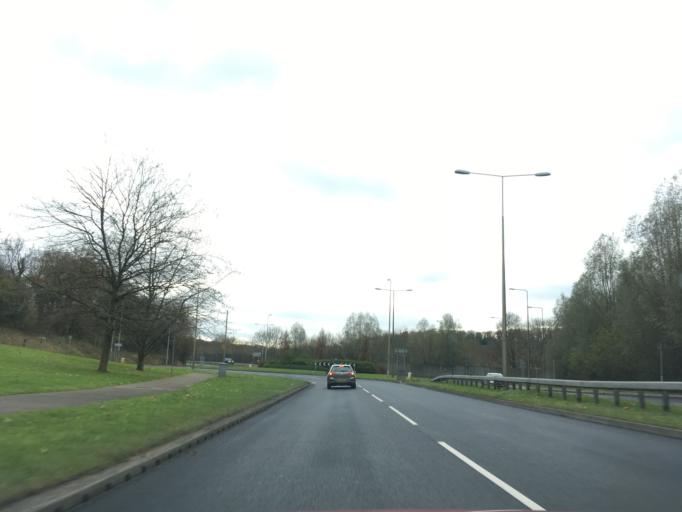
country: GB
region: Wales
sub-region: Newport
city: Langstone
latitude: 51.5986
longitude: -2.9258
